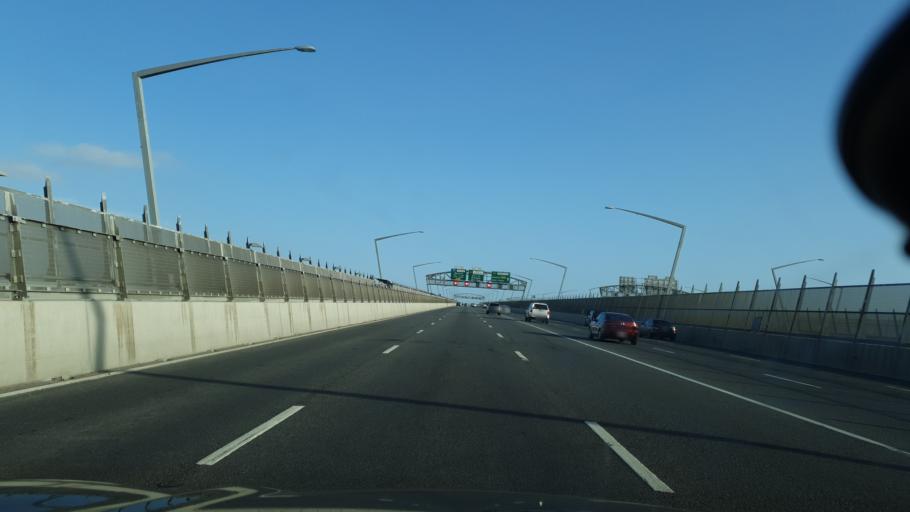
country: AU
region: Queensland
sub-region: Brisbane
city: Cannon Hill
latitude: -27.4374
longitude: 153.0972
